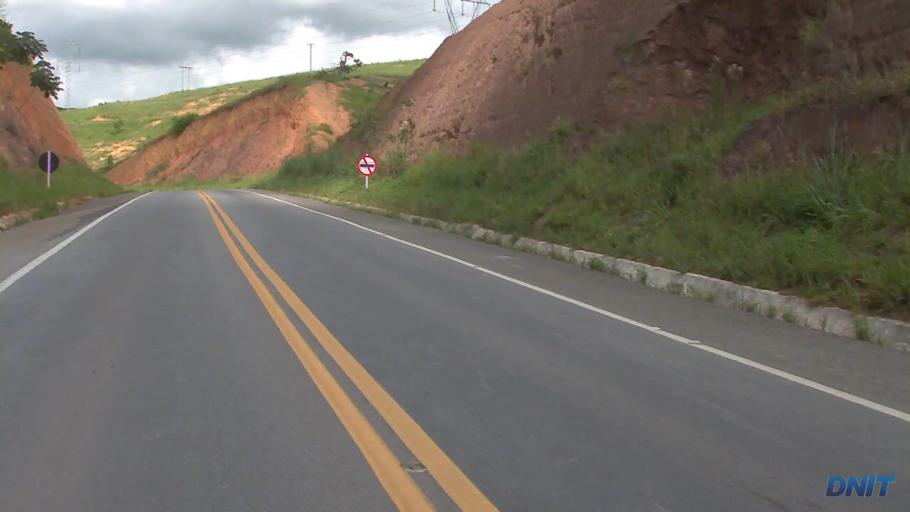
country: BR
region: Minas Gerais
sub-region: Belo Oriente
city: Belo Oriente
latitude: -19.0961
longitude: -42.1962
